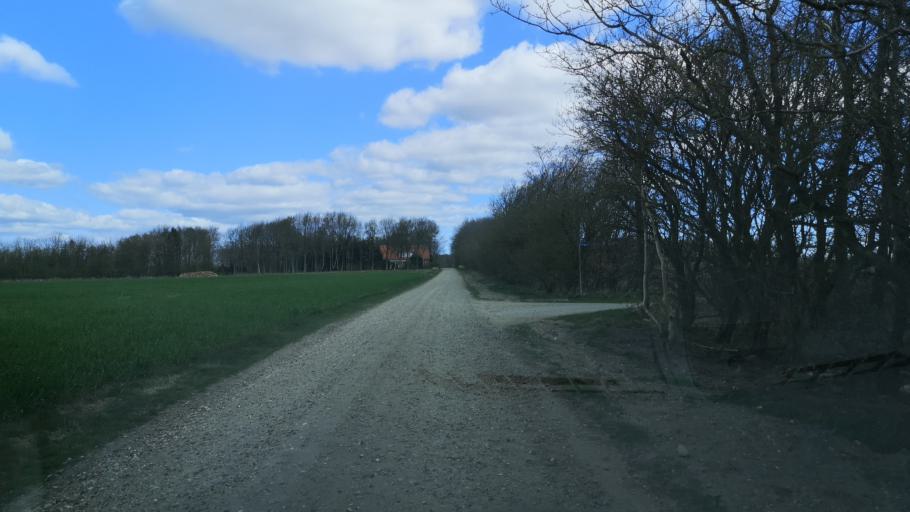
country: DK
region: Central Jutland
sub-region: Ringkobing-Skjern Kommune
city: Skjern
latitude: 55.9861
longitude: 8.5152
